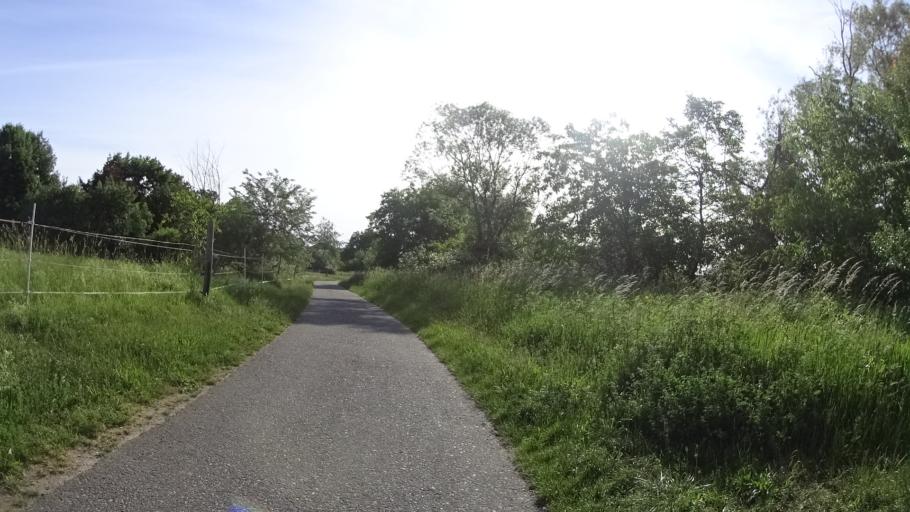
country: DE
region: Bavaria
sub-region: Regierungsbezirk Unterfranken
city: Kahl am Main
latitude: 50.0461
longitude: 9.0109
